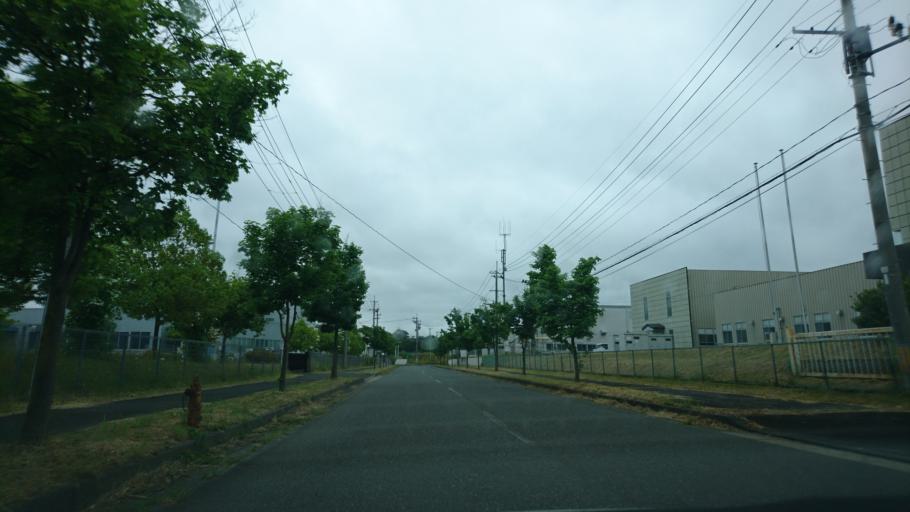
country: JP
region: Iwate
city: Ichinoseki
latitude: 38.9190
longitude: 141.1663
